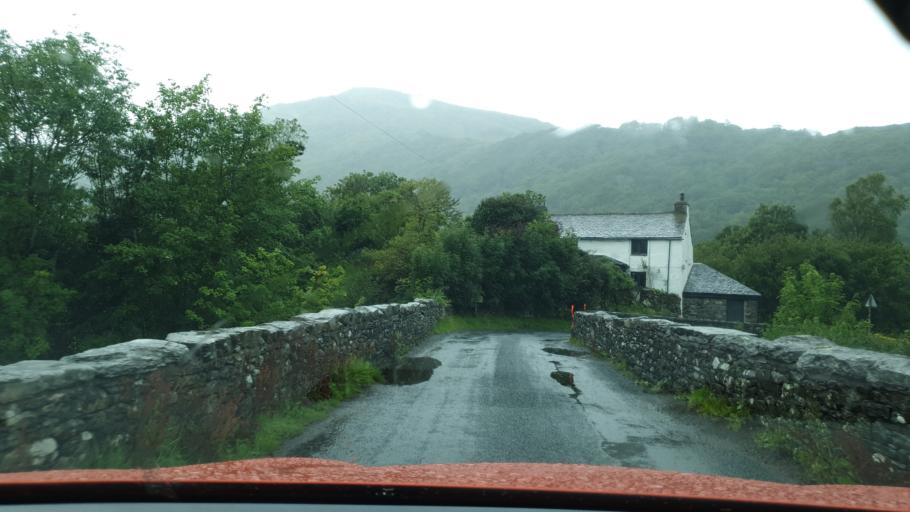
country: GB
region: England
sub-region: Cumbria
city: Millom
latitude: 54.3265
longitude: -3.2368
